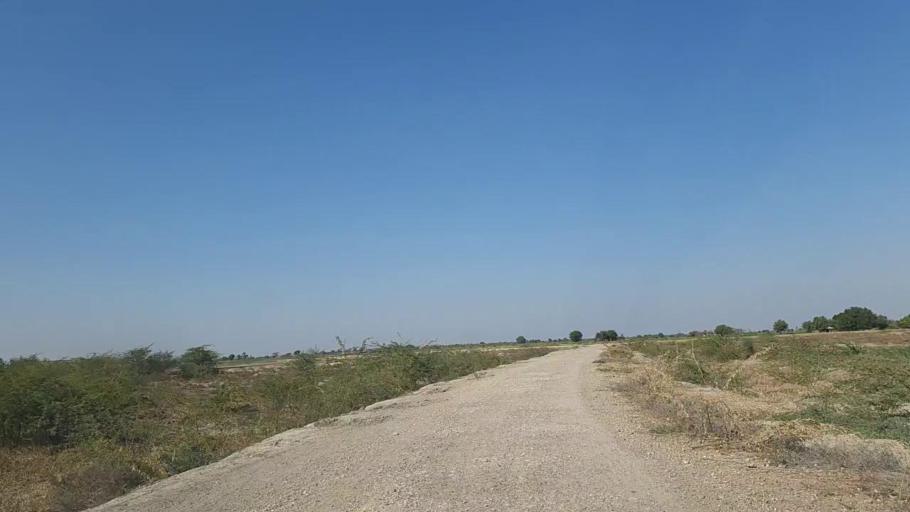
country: PK
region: Sindh
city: Naukot
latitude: 25.0201
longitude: 69.3587
